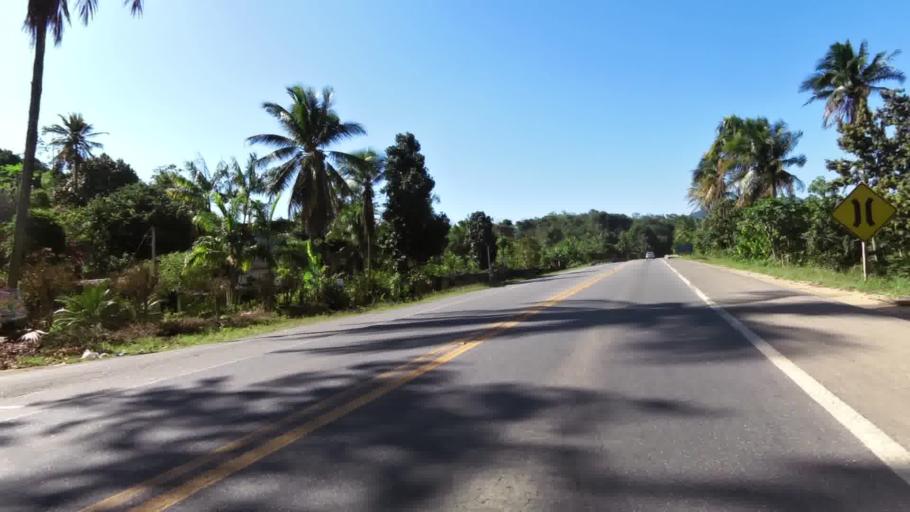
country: BR
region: Espirito Santo
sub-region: Iconha
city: Iconha
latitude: -20.8149
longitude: -40.8412
